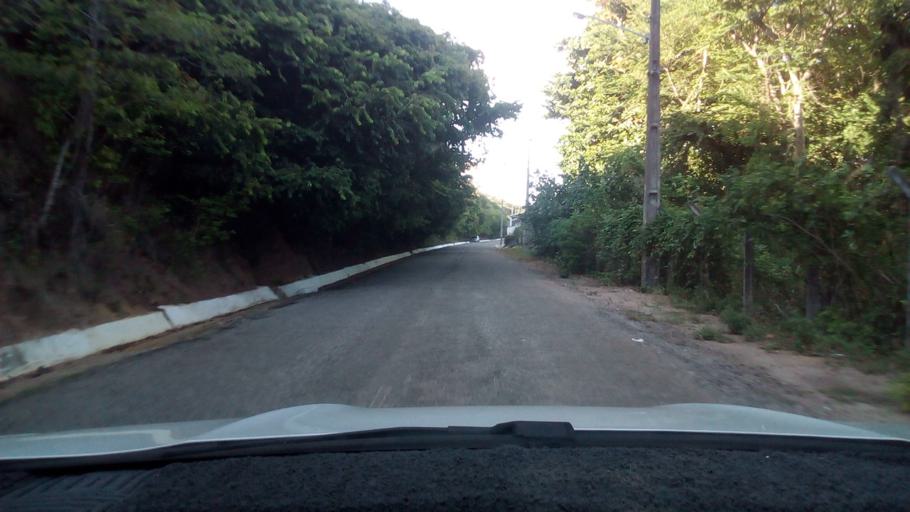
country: BR
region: Paraiba
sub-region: Joao Pessoa
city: Joao Pessoa
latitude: -7.1631
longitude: -34.7973
